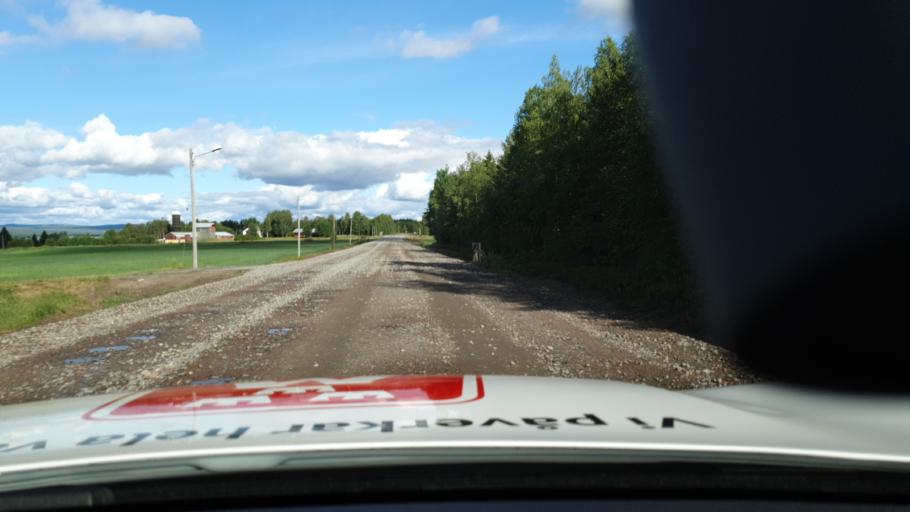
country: SE
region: Norrbotten
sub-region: Bodens Kommun
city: Boden
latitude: 65.8837
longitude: 21.3977
